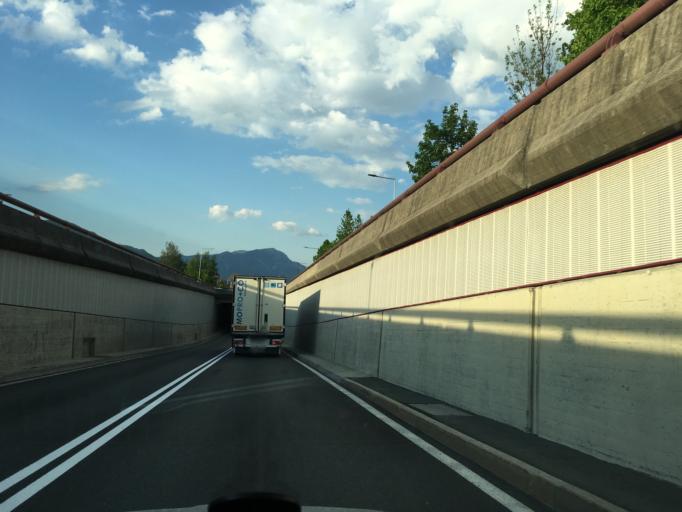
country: AT
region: Tyrol
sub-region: Politischer Bezirk Kitzbuhel
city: Sankt Johann in Tirol
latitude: 47.5213
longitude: 12.4197
